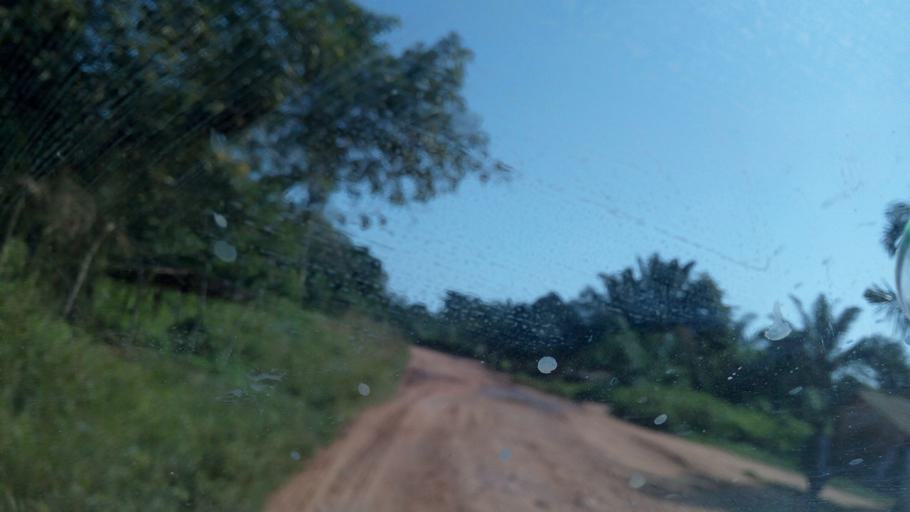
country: BI
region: Bururi
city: Rumonge
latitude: -3.8372
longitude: 29.0977
